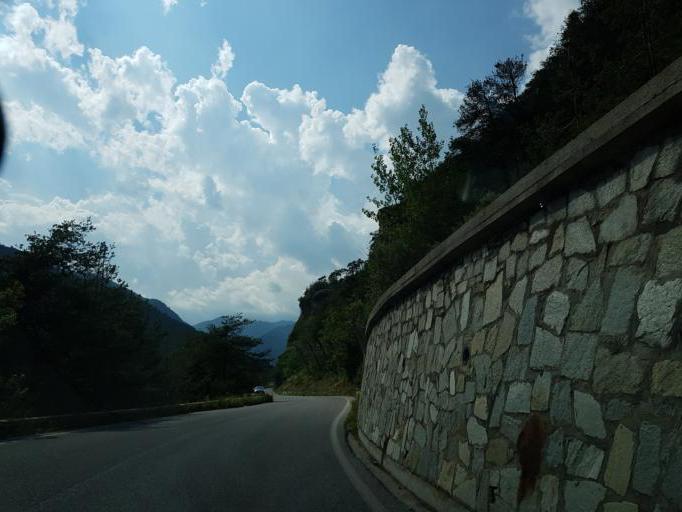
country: IT
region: Piedmont
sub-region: Provincia di Cuneo
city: Macra
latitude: 44.4991
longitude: 7.1714
